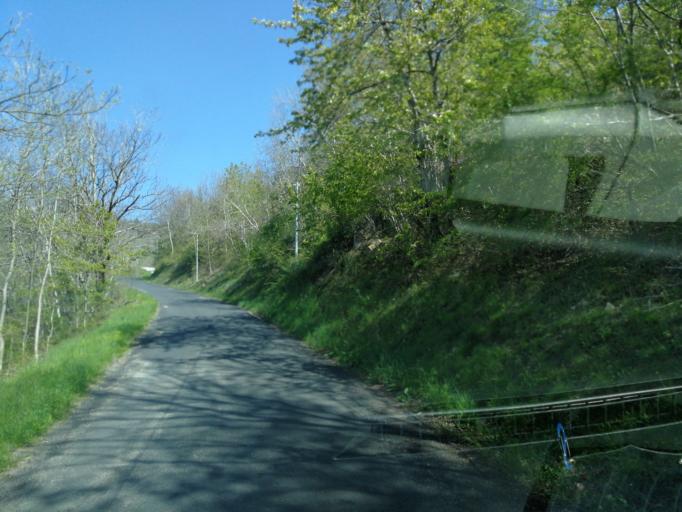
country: FR
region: Rhone-Alpes
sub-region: Departement de l'Ardeche
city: Le Cheylard
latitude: 44.9309
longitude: 4.4246
